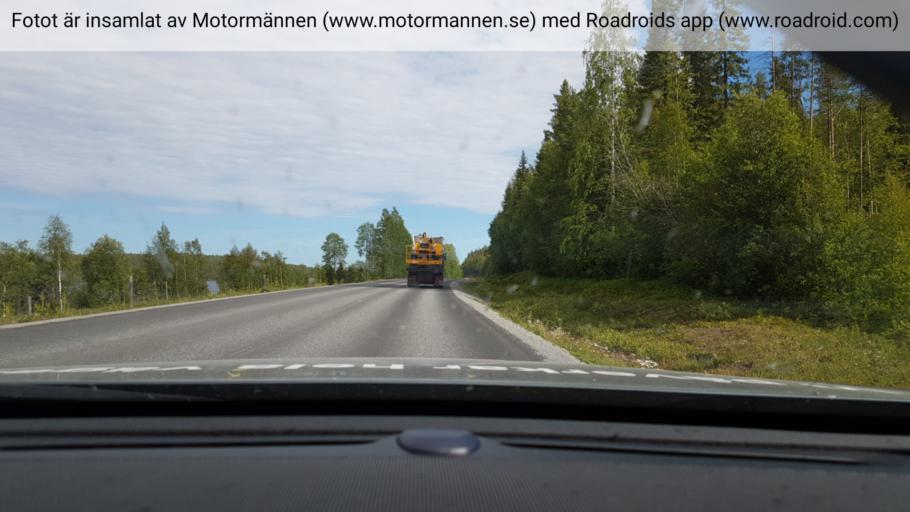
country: SE
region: Vaesterbotten
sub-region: Lycksele Kommun
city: Soderfors
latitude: 64.8529
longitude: 17.9469
